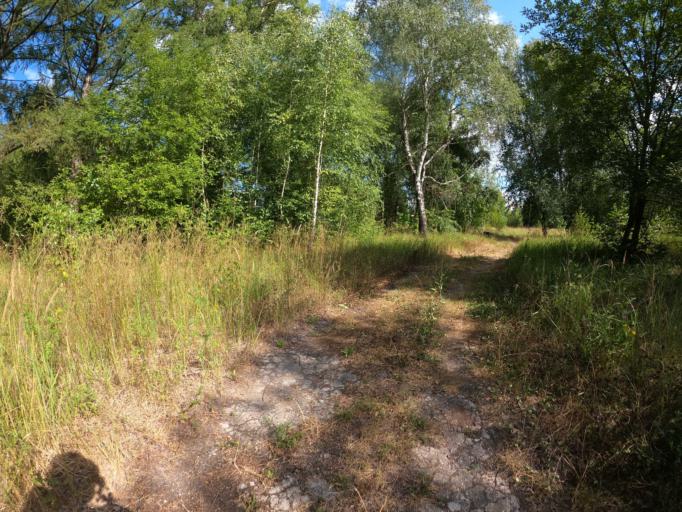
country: RU
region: Moskovskaya
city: Konobeyevo
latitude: 55.3903
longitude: 38.7088
